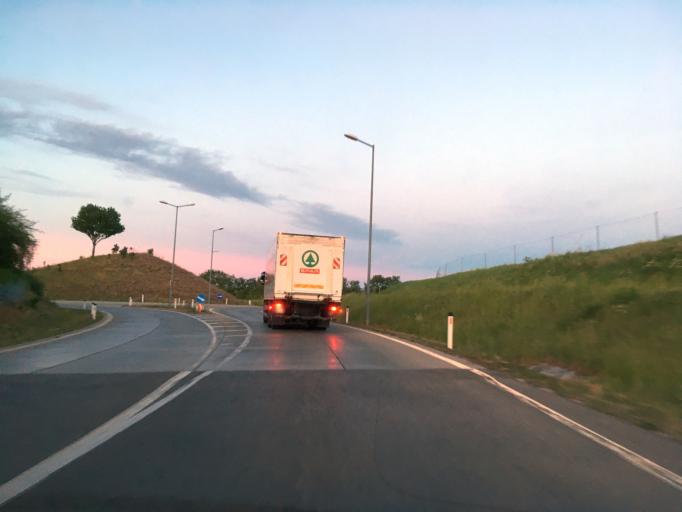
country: AT
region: Lower Austria
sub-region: Politischer Bezirk Wien-Umgebung
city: Schwechat
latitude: 48.1223
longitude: 16.4792
